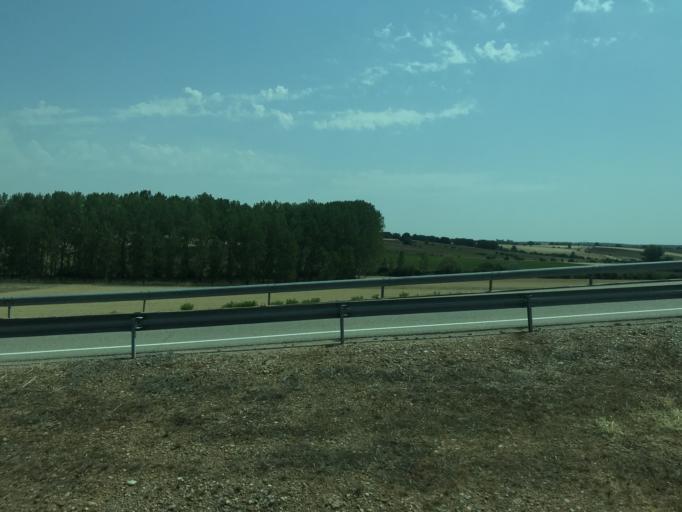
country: ES
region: Castille and Leon
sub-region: Provincia de Segovia
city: Fresno de la Fuente
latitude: 41.3688
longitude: -3.6400
